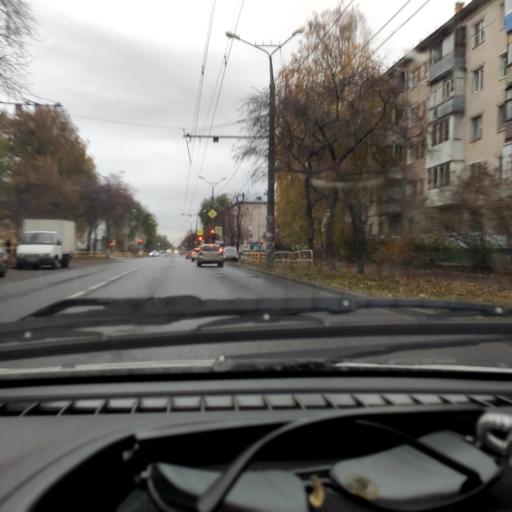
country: RU
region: Samara
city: Tol'yatti
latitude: 53.5155
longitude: 49.4172
